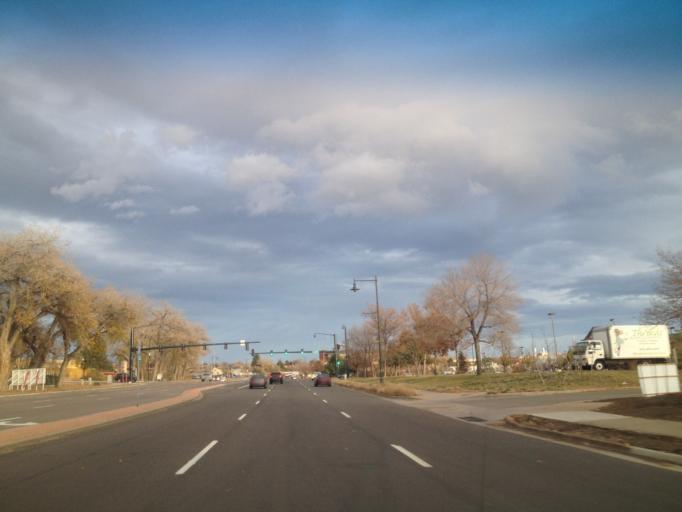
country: US
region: Colorado
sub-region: Adams County
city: Westminster
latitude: 39.8564
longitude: -105.0599
